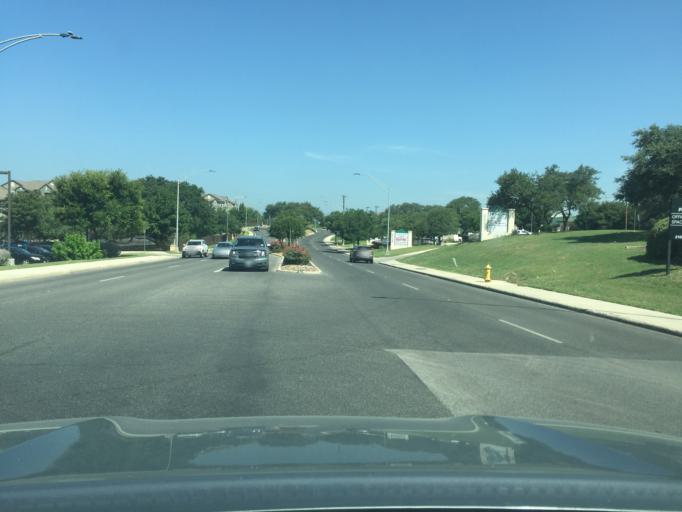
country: US
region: Texas
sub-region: Bexar County
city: Hollywood Park
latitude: 29.6434
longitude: -98.4903
